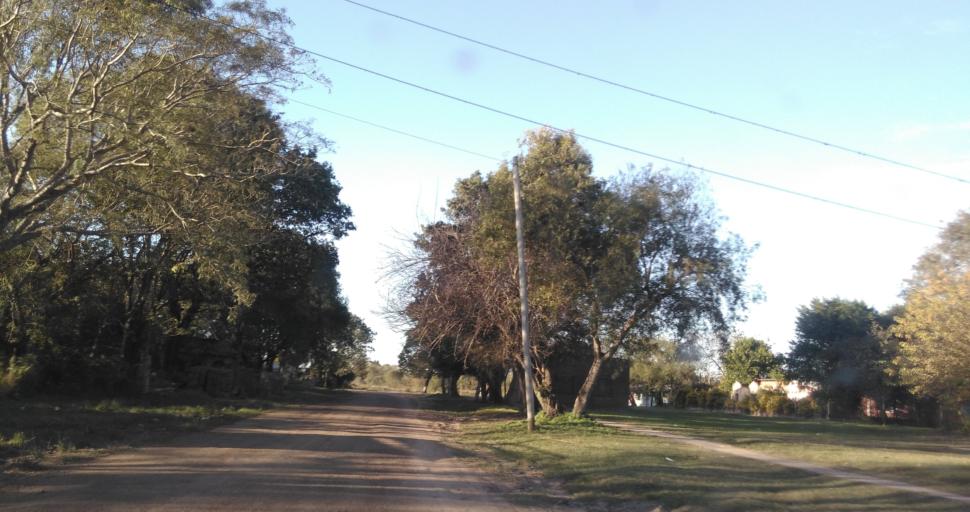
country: AR
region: Chaco
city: Colonia Benitez
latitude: -27.3310
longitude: -58.9449
